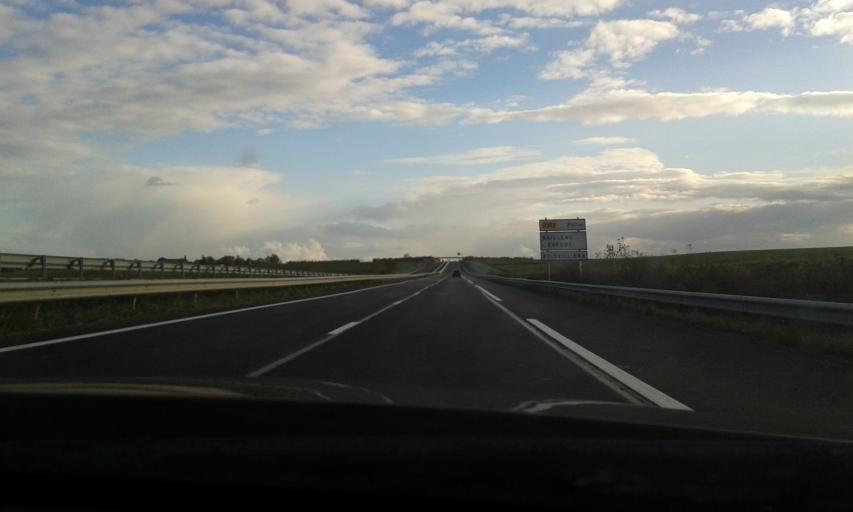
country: FR
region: Centre
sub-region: Departement d'Eure-et-Loir
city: Leves
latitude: 48.5174
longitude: 1.4591
